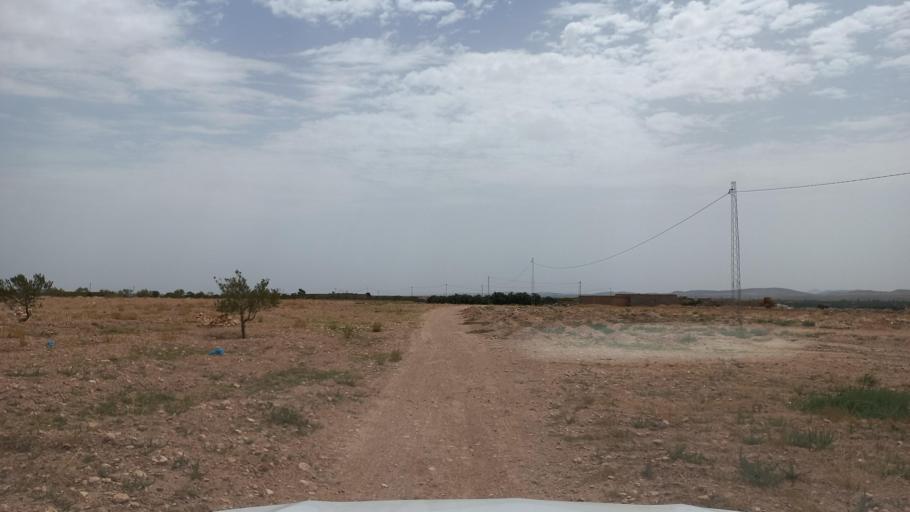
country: TN
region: Al Qasrayn
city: Kasserine
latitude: 35.2907
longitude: 9.0027
